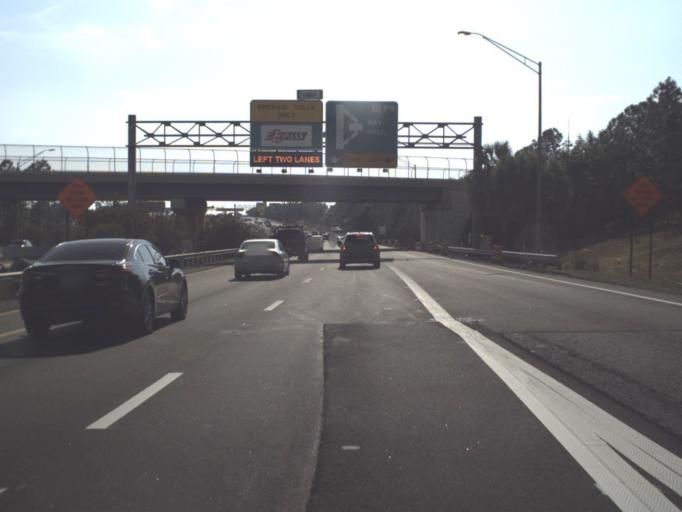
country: US
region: Florida
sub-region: Orange County
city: Orlovista
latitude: 28.5491
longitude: -81.4825
